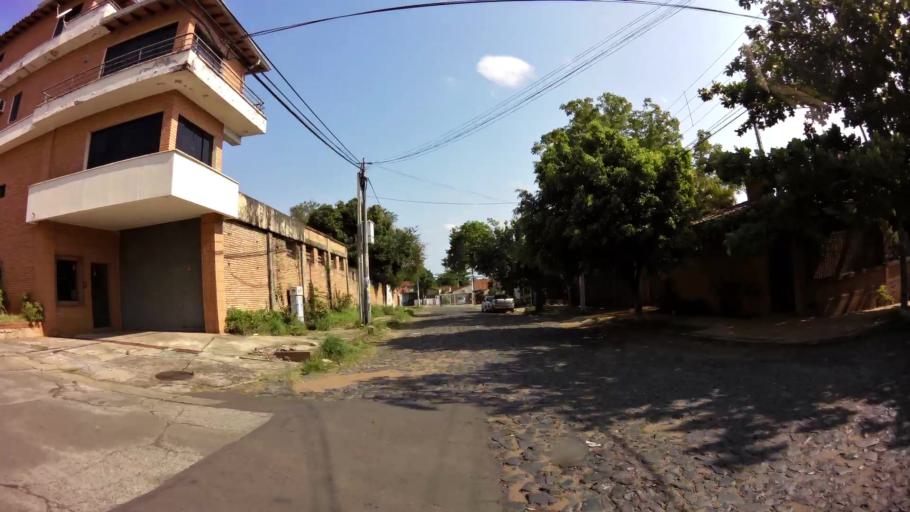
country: PY
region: Asuncion
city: Asuncion
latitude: -25.3242
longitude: -57.6323
